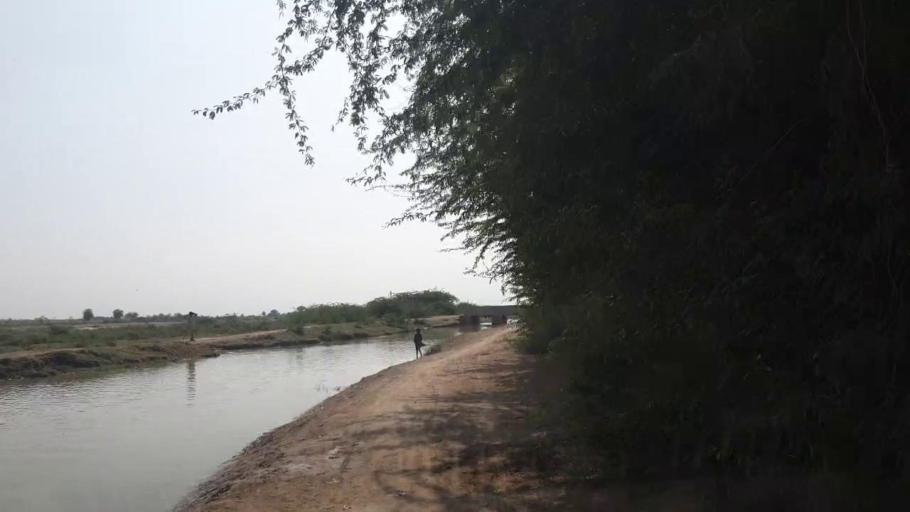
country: PK
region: Sindh
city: Kadhan
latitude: 24.5054
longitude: 68.8500
